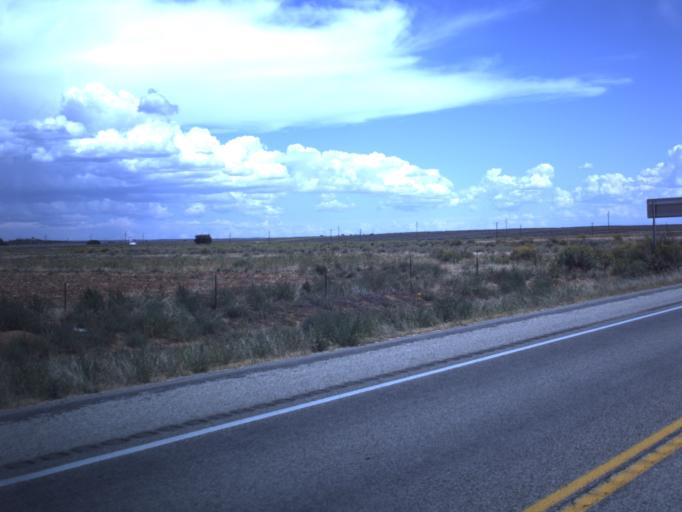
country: US
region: Utah
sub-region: San Juan County
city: Blanding
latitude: 37.5736
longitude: -109.4843
